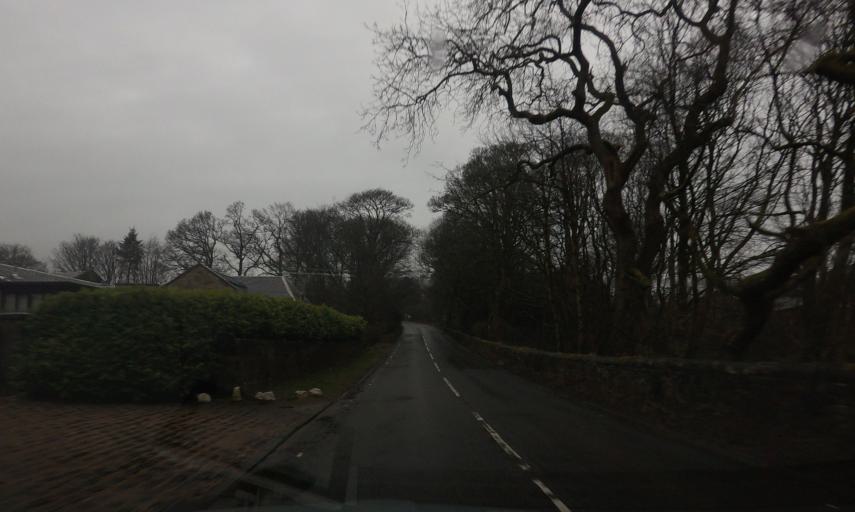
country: GB
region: Scotland
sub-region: East Dunbartonshire
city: Milngavie
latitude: 55.9428
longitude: -4.3490
